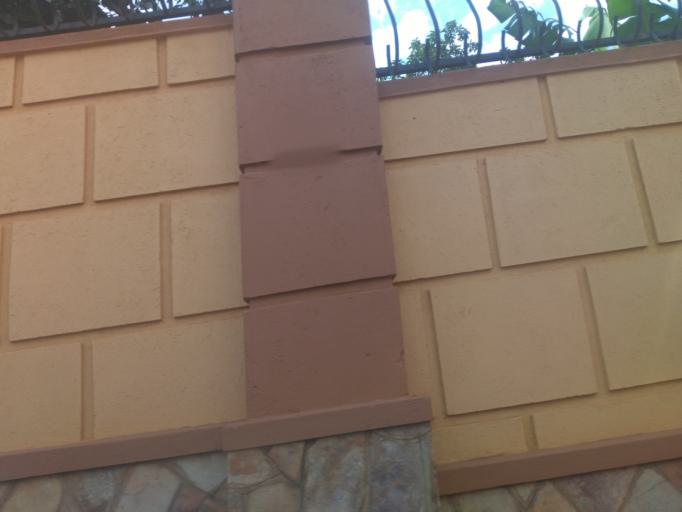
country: UG
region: Central Region
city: Kampala Central Division
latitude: 0.3577
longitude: 32.5840
